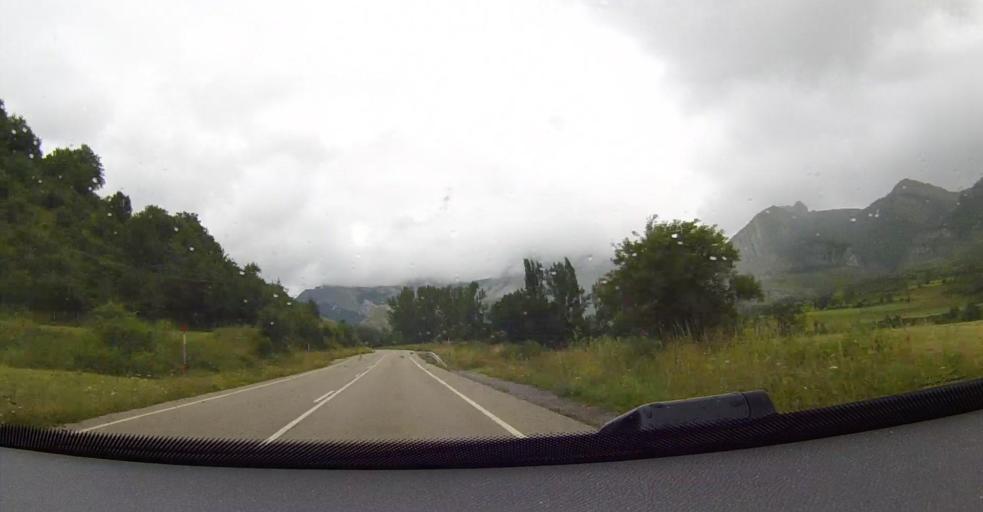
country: ES
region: Castille and Leon
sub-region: Provincia de Leon
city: Buron
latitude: 43.0347
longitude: -5.0788
